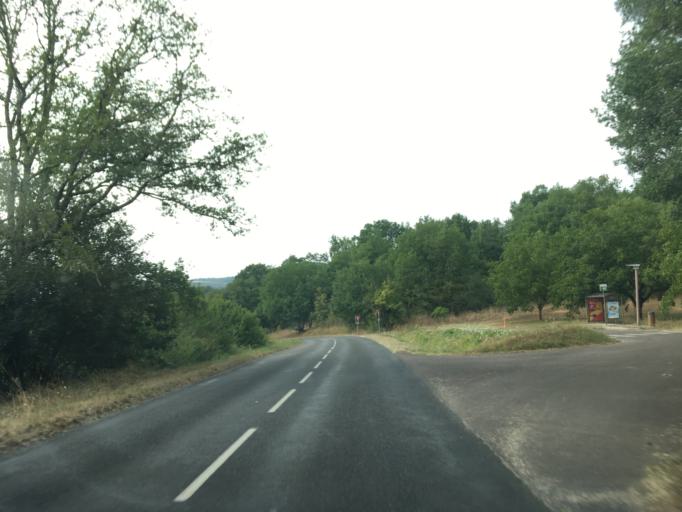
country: FR
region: Midi-Pyrenees
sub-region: Departement du Lot
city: Souillac
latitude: 44.8483
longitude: 1.5415
